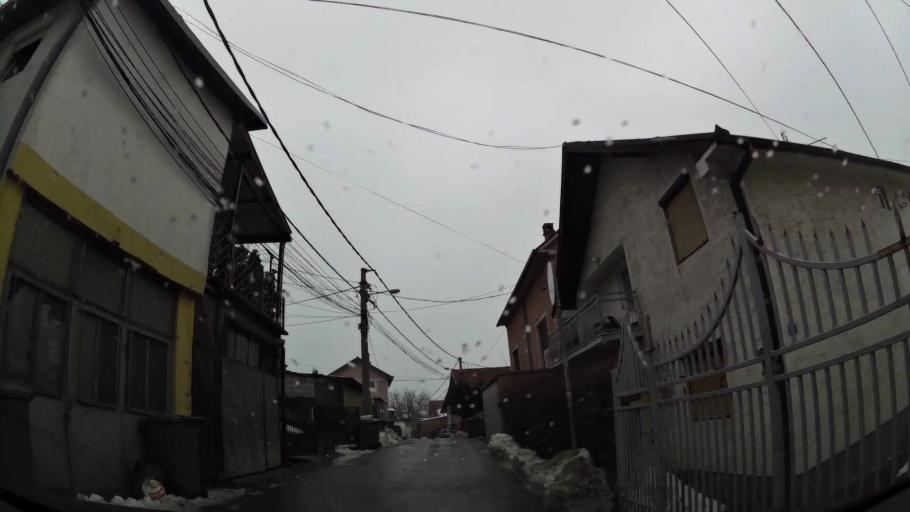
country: RS
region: Central Serbia
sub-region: Belgrade
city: Zvezdara
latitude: 44.7745
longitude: 20.5225
